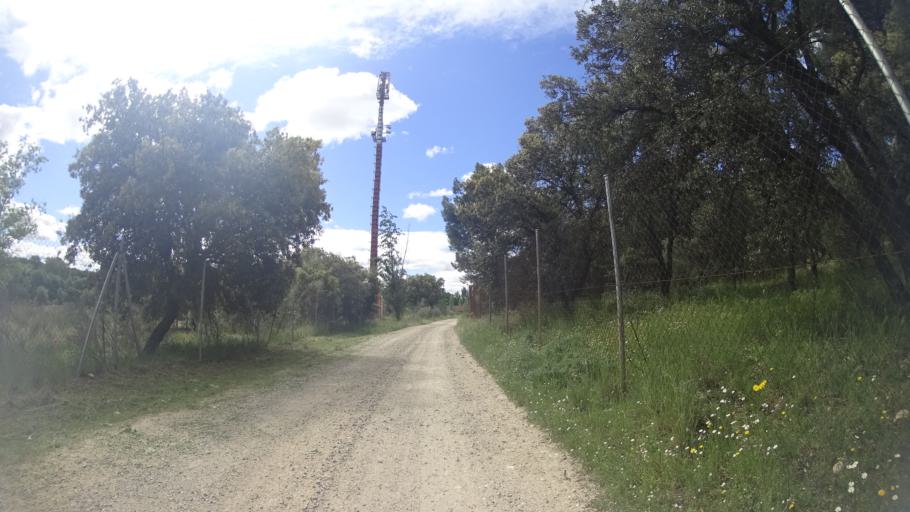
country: ES
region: Madrid
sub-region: Provincia de Madrid
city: Brunete
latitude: 40.4076
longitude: -3.9495
